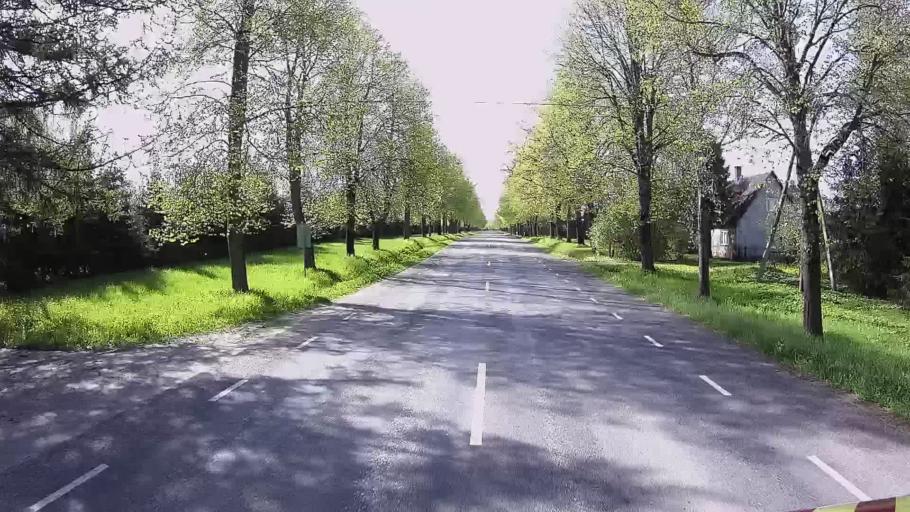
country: EE
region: Polvamaa
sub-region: Polva linn
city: Polva
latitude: 58.2001
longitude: 27.0774
